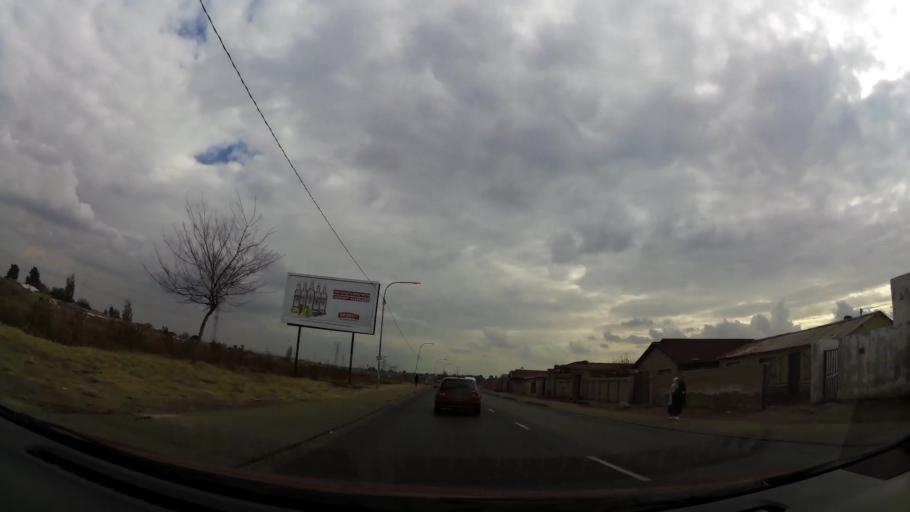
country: ZA
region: Gauteng
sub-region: City of Johannesburg Metropolitan Municipality
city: Soweto
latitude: -26.2398
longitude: 27.8530
